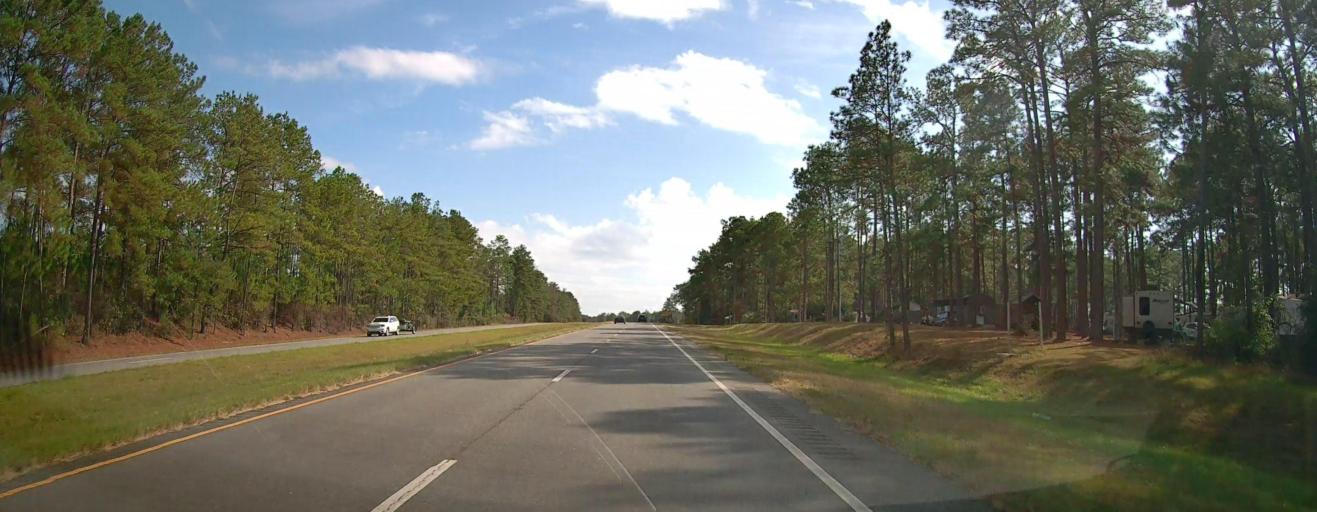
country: US
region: Georgia
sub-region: Thomas County
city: Thomasville
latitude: 30.9538
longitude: -84.0262
